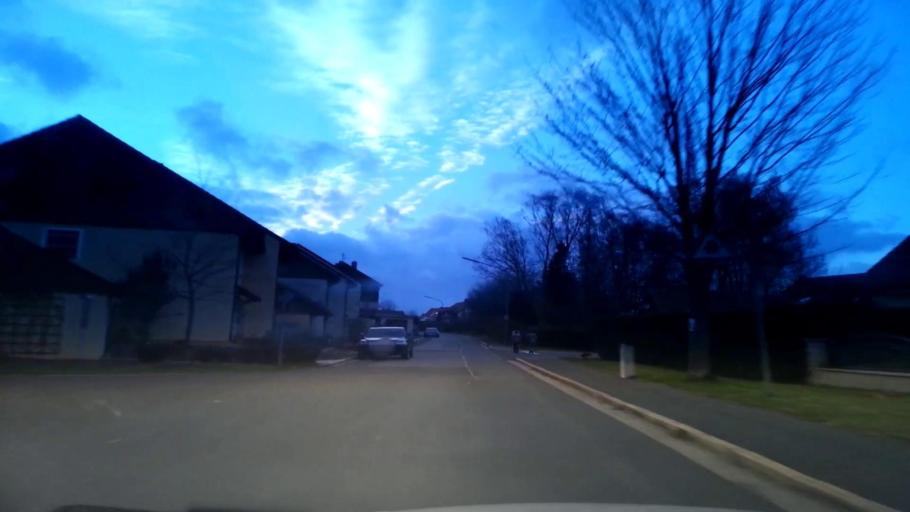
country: DE
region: Bavaria
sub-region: Upper Palatinate
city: Waldershof
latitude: 49.9747
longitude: 12.0660
